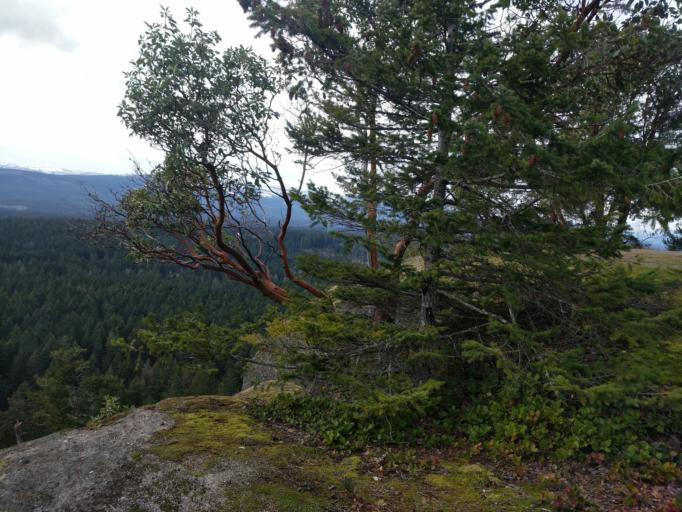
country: CA
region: British Columbia
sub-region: Regional District of Nanaimo
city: Parksville
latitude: 49.2943
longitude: -124.3240
